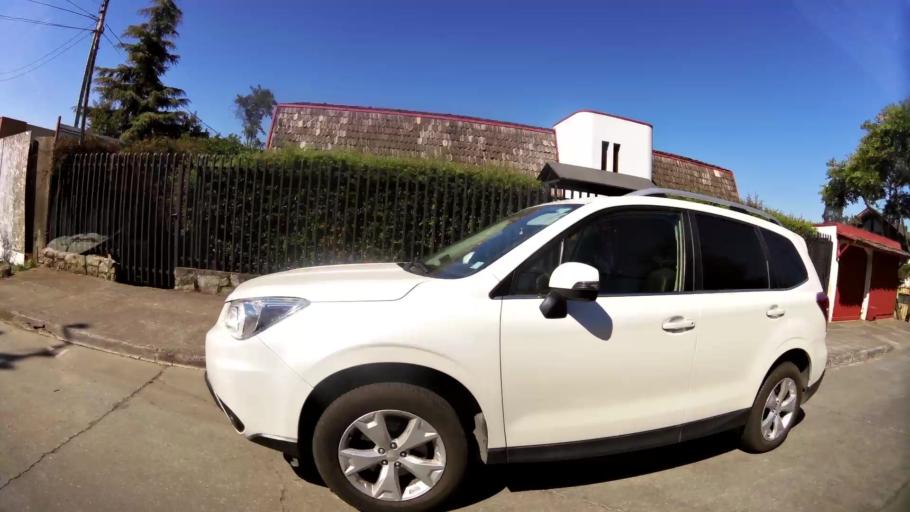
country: CL
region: Biobio
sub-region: Provincia de Concepcion
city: Concepcion
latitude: -36.7933
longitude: -73.0597
